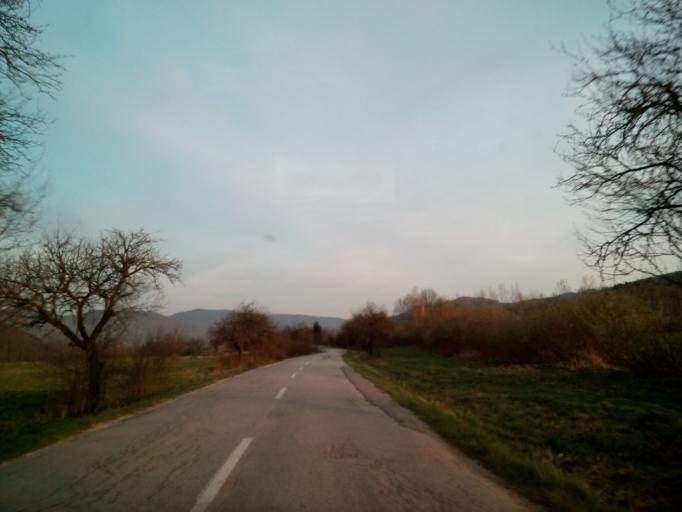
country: SK
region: Kosicky
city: Dobsina
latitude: 48.6983
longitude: 20.3068
